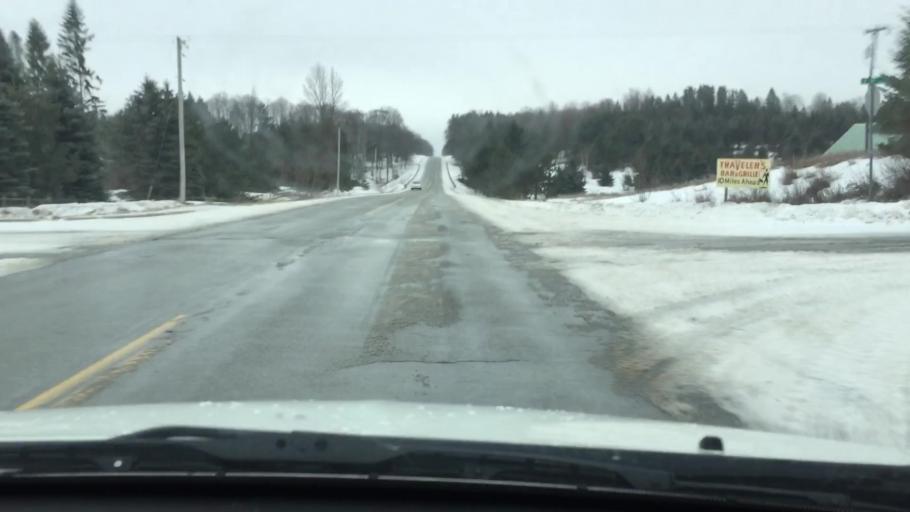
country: US
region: Michigan
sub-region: Wexford County
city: Cadillac
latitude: 44.1795
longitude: -85.4055
